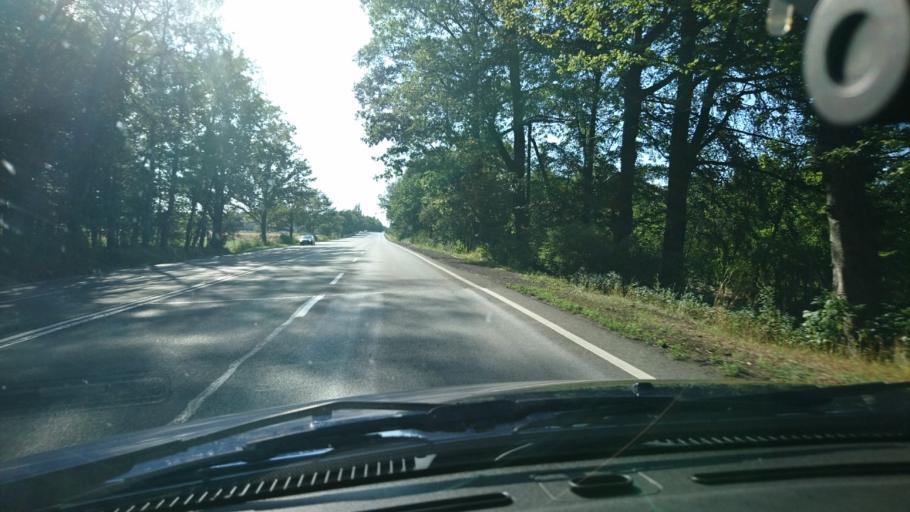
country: PL
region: Silesian Voivodeship
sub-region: Gliwice
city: Gliwice
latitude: 50.3130
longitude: 18.7073
